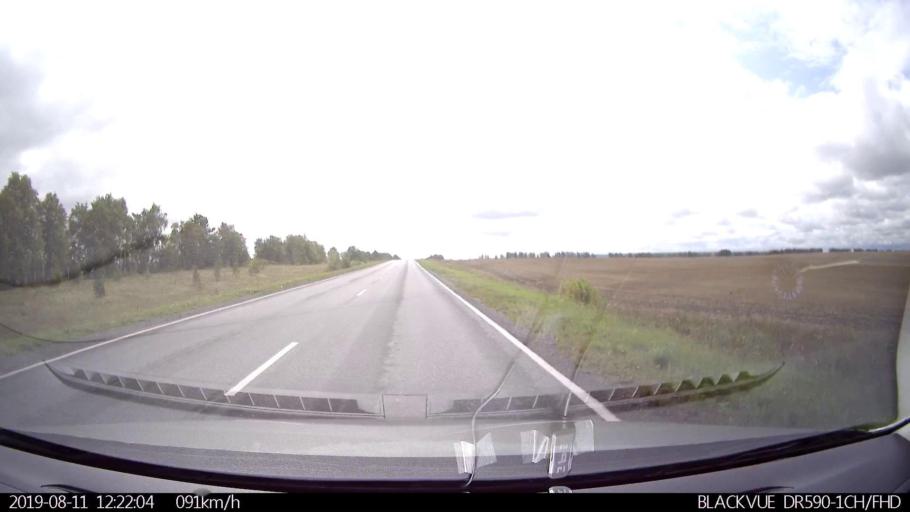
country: RU
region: Ulyanovsk
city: Ignatovka
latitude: 53.9133
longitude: 47.9557
